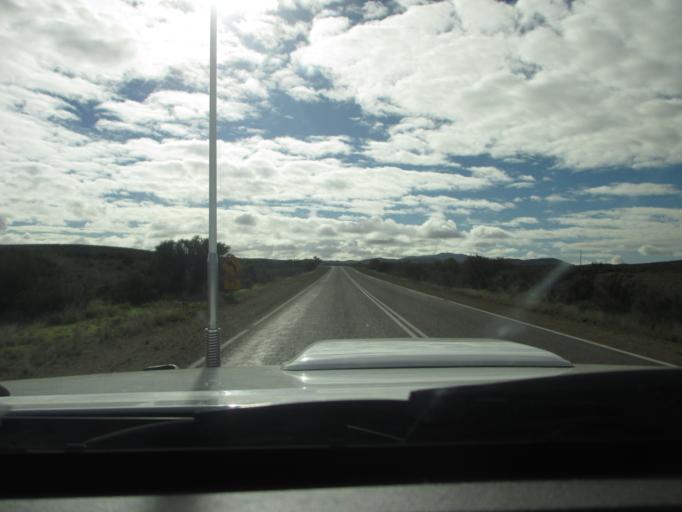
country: AU
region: South Australia
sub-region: Flinders Ranges
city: Quorn
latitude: -32.3262
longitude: 138.4787
